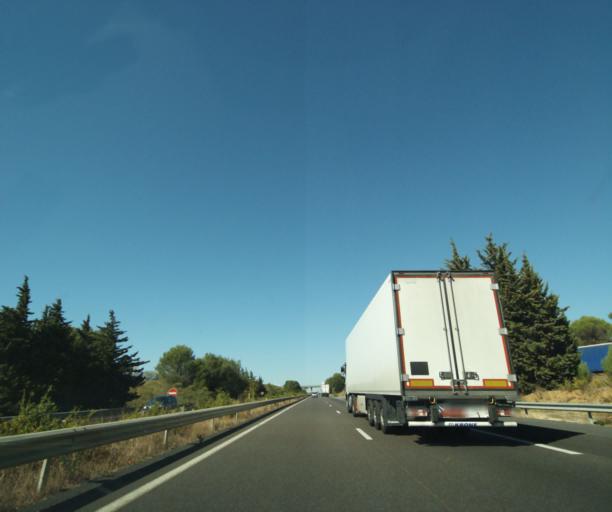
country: FR
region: Languedoc-Roussillon
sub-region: Departement du Gard
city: Garons
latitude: 43.7589
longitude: 4.4267
